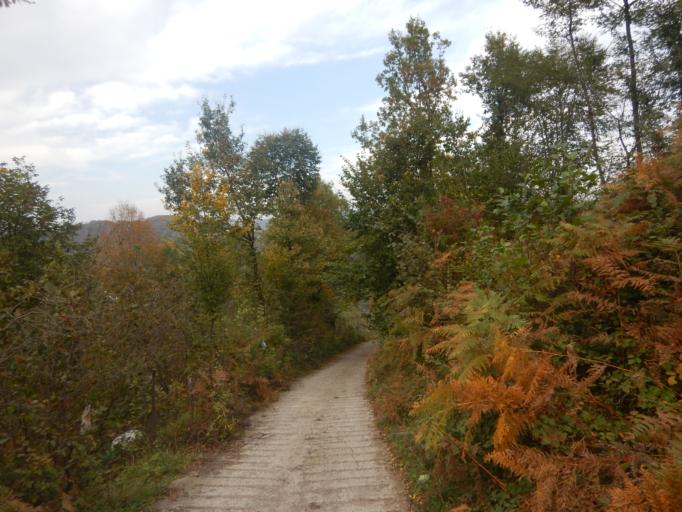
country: TR
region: Ordu
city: Golkoy
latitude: 40.6904
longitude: 37.5840
